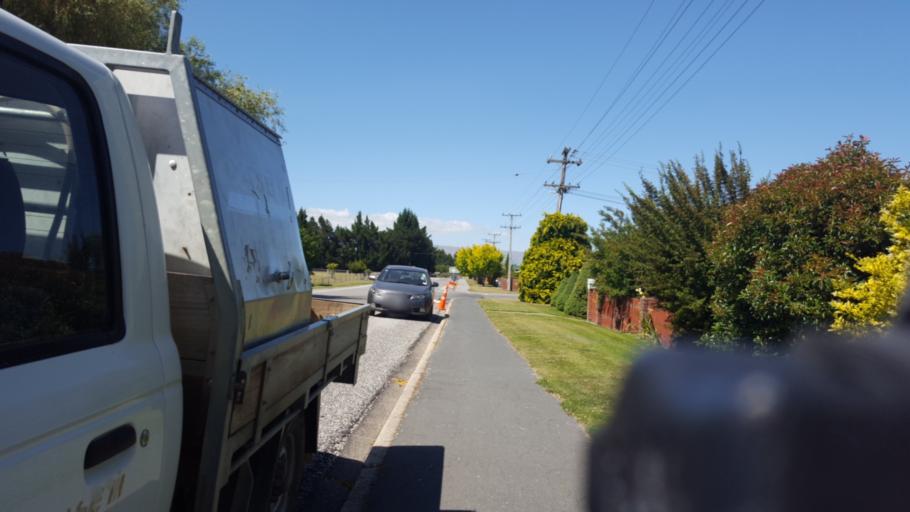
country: NZ
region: Otago
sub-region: Dunedin City
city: Dunedin
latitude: -45.1287
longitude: 170.1060
